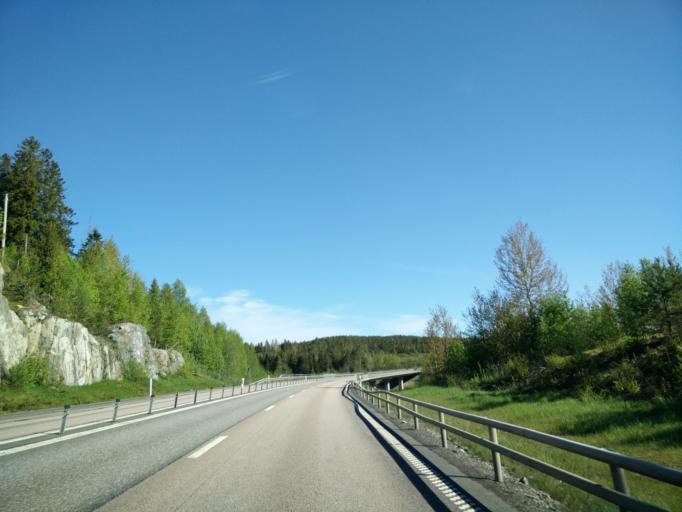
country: SE
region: Vaesternorrland
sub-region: Haernoesands Kommun
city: Haernoesand
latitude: 62.8326
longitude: 17.9677
